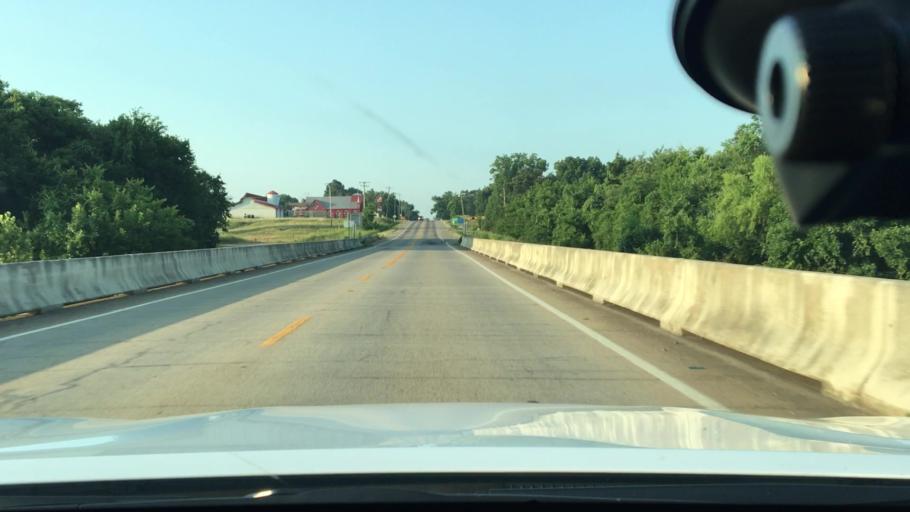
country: US
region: Arkansas
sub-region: Johnson County
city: Clarksville
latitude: 35.3910
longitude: -93.5303
